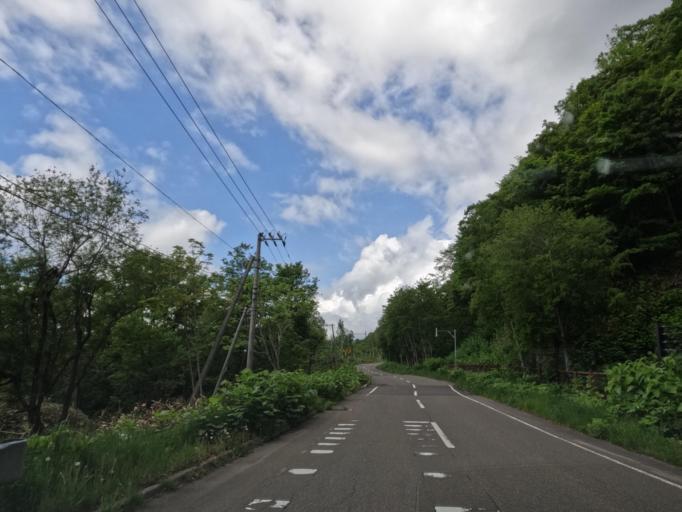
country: JP
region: Hokkaido
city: Tobetsu
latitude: 43.4830
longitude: 141.6032
